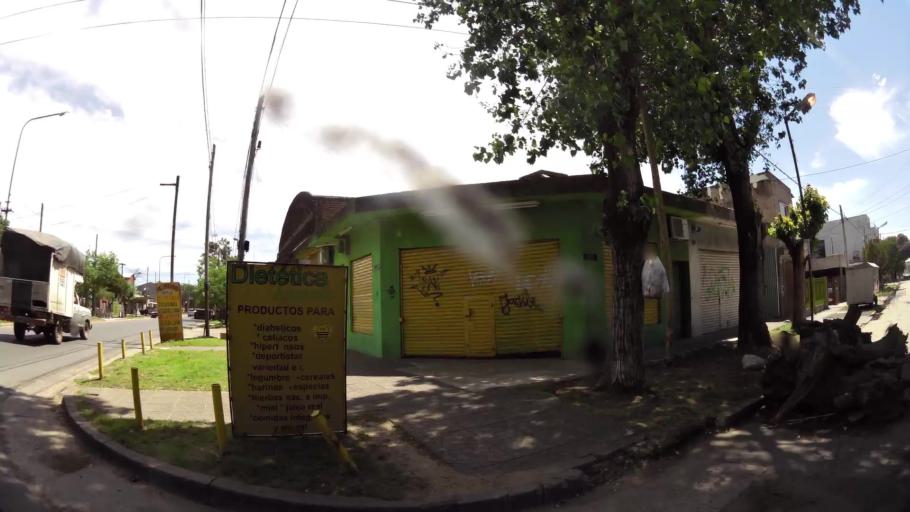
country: AR
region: Buenos Aires
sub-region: Partido de Quilmes
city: Quilmes
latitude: -34.7475
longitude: -58.2936
